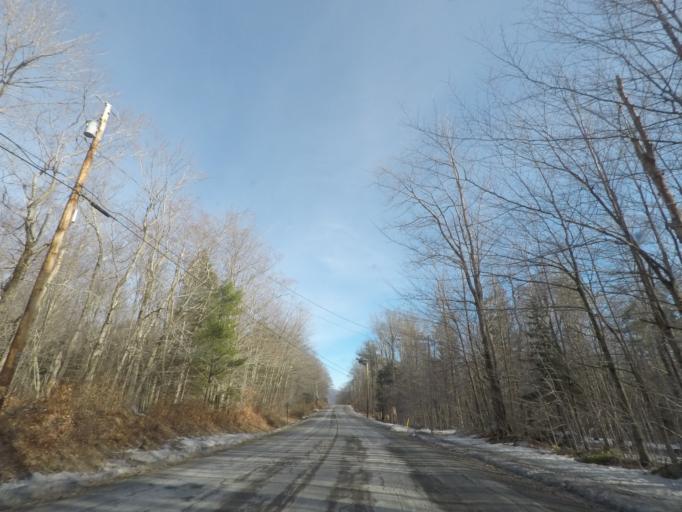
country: US
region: New York
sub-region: Rensselaer County
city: Hoosick Falls
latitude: 42.7396
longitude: -73.3935
